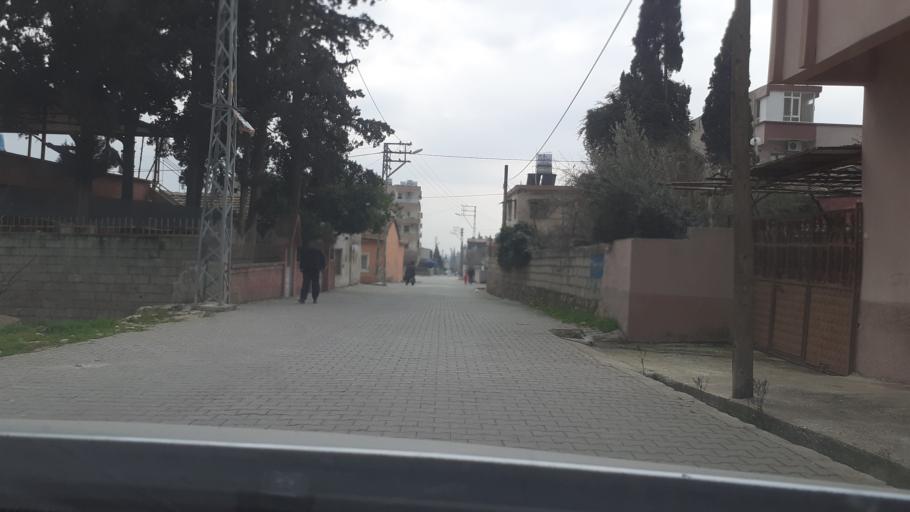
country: TR
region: Hatay
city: Kirikhan
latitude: 36.4953
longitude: 36.3528
